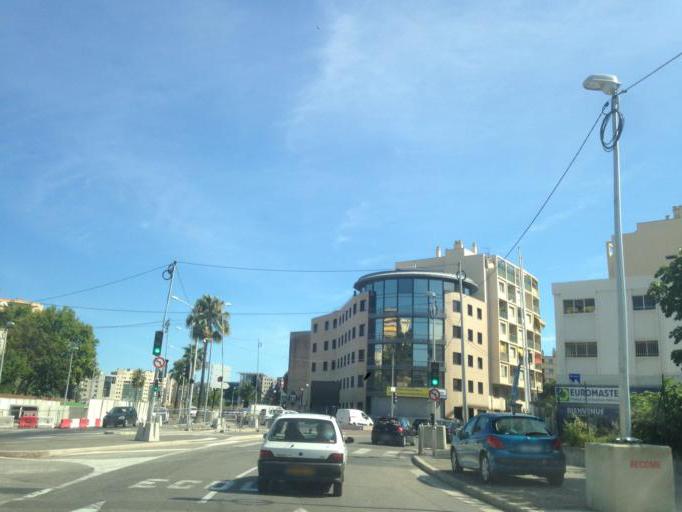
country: FR
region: Provence-Alpes-Cote d'Azur
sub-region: Departement des Alpes-Maritimes
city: Saint-Laurent-du-Var
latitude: 43.6719
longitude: 7.2098
